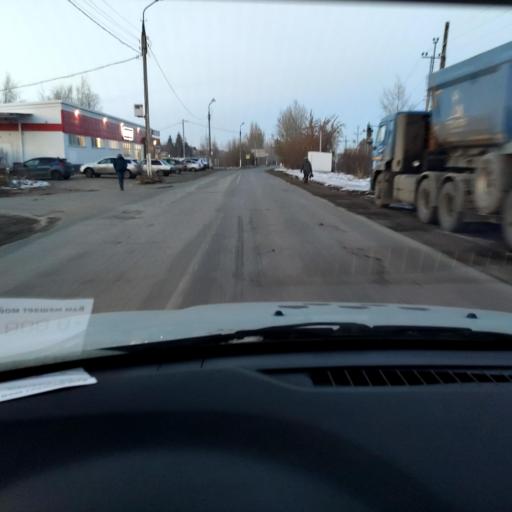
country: RU
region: Samara
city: Tol'yatti
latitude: 53.5563
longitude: 49.3940
